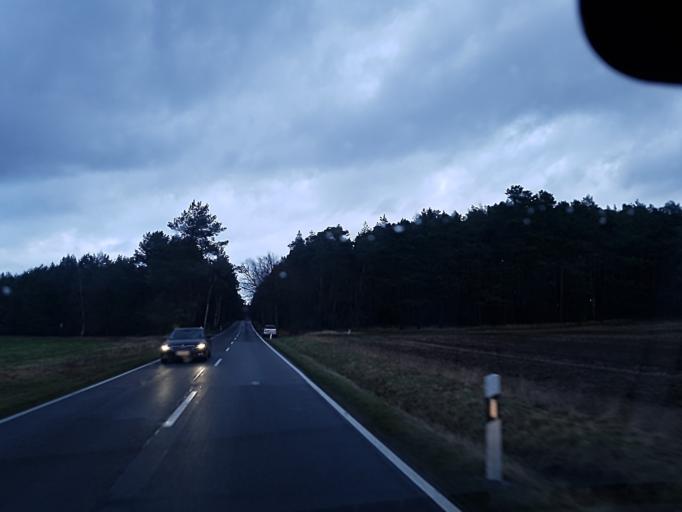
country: DE
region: Brandenburg
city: Plessa
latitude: 51.5446
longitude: 13.6690
